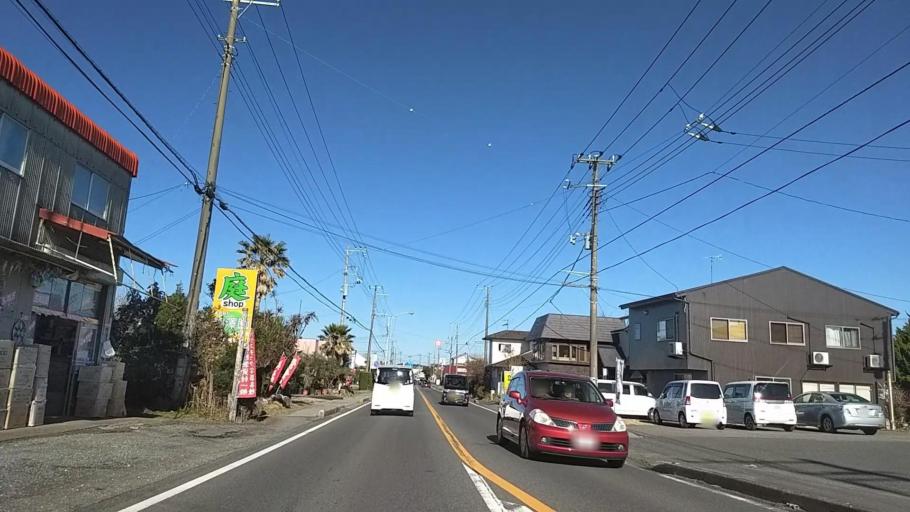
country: JP
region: Chiba
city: Ohara
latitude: 35.2899
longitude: 140.3933
